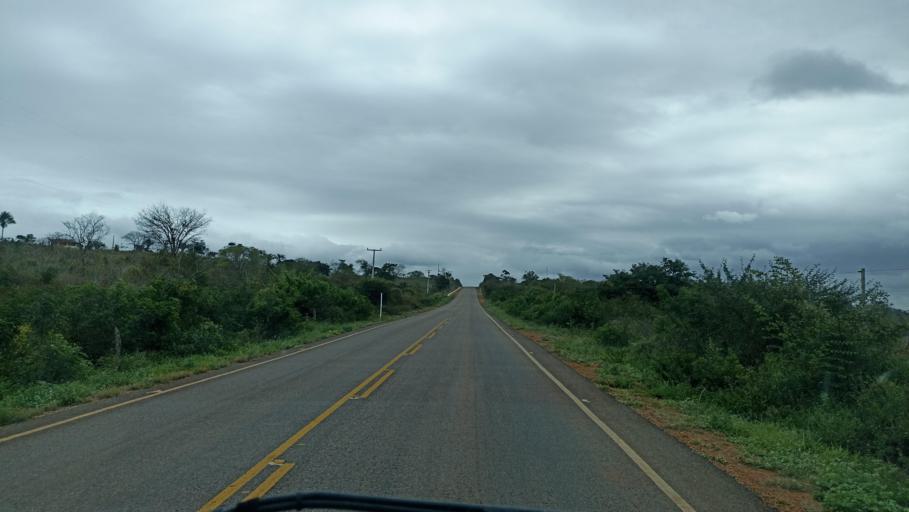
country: BR
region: Bahia
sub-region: Andarai
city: Vera Cruz
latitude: -12.9949
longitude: -40.9974
